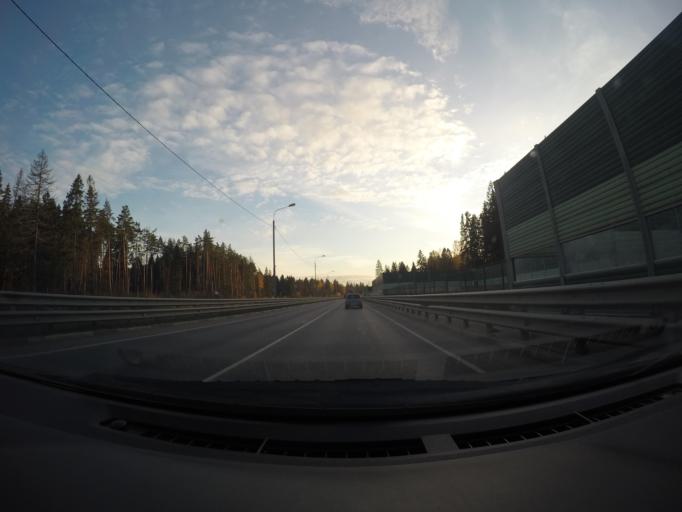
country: RU
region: Moskovskaya
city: Firsanovka
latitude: 55.9546
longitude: 37.2592
